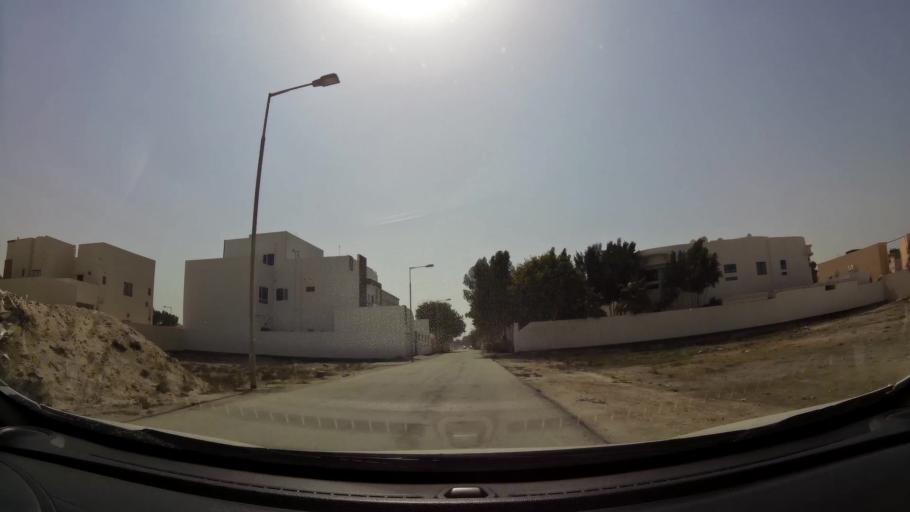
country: BH
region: Northern
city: Madinat `Isa
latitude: 26.1950
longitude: 50.4664
